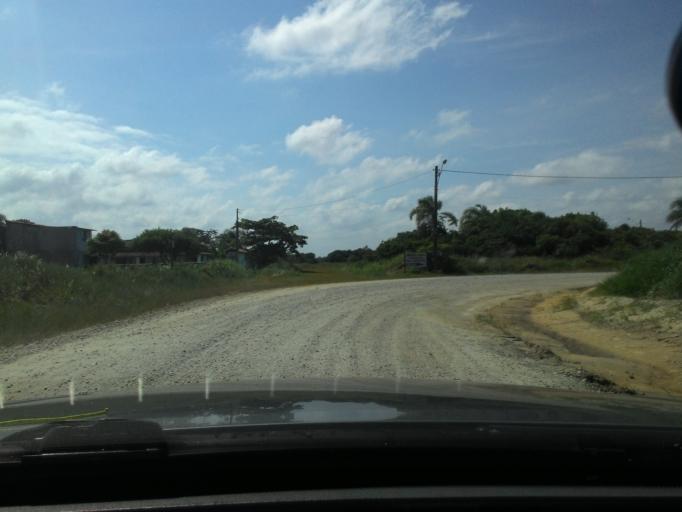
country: BR
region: Sao Paulo
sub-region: Iguape
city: Iguape
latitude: -24.8508
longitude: -47.6992
